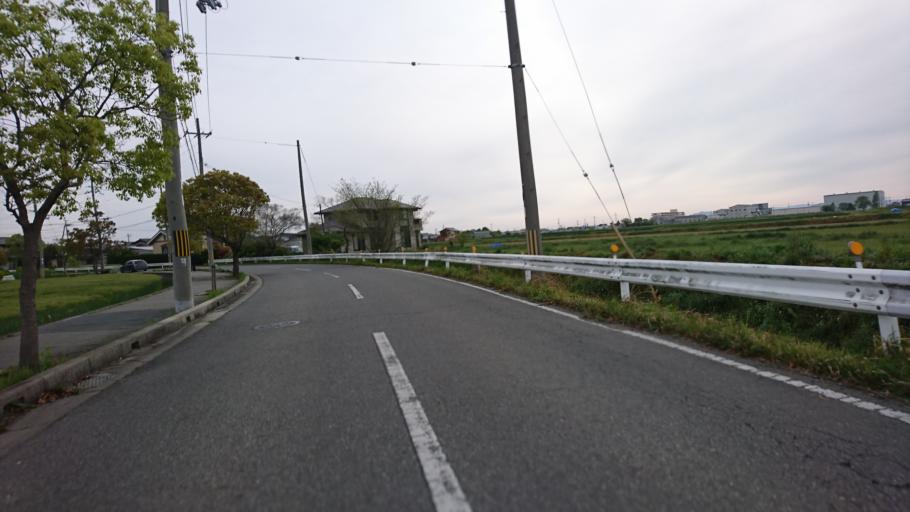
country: JP
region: Hyogo
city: Kakogawacho-honmachi
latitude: 34.7584
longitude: 134.9075
